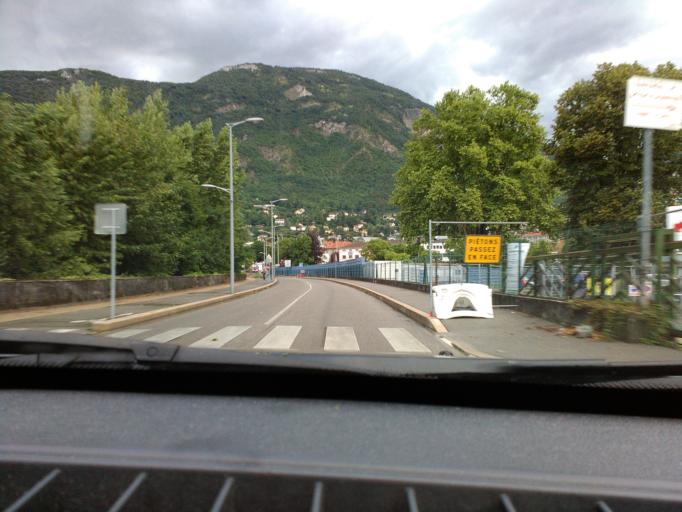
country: FR
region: Rhone-Alpes
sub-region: Departement de l'Isere
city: La Tronche
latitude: 45.1990
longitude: 5.7435
